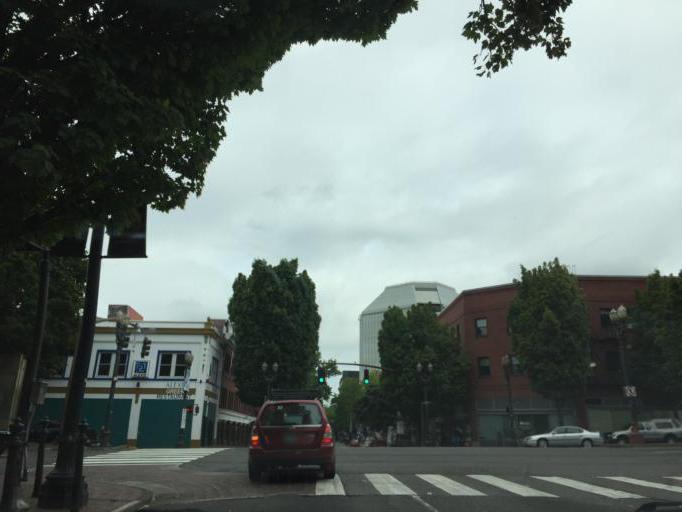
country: US
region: Oregon
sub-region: Multnomah County
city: Portland
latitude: 45.5228
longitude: -122.6724
